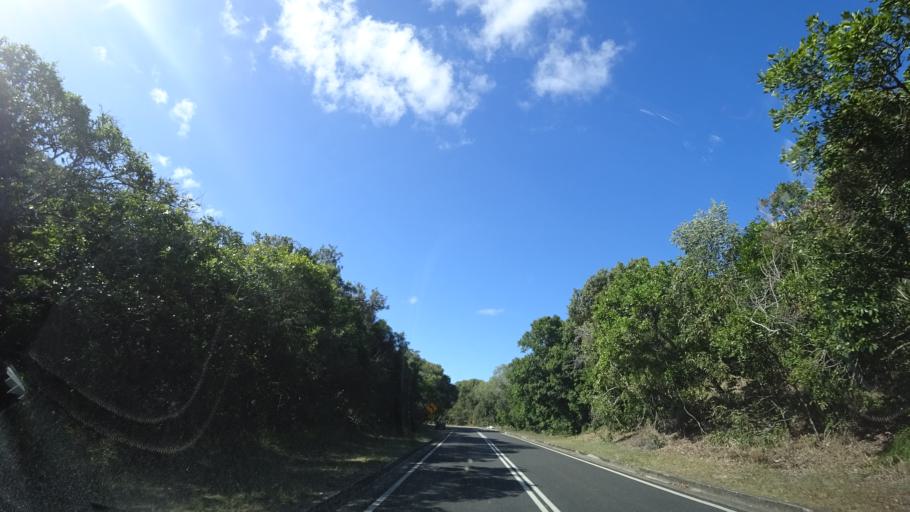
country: AU
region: Queensland
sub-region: Sunshine Coast
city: Mooloolaba
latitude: -26.6301
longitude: 153.1002
